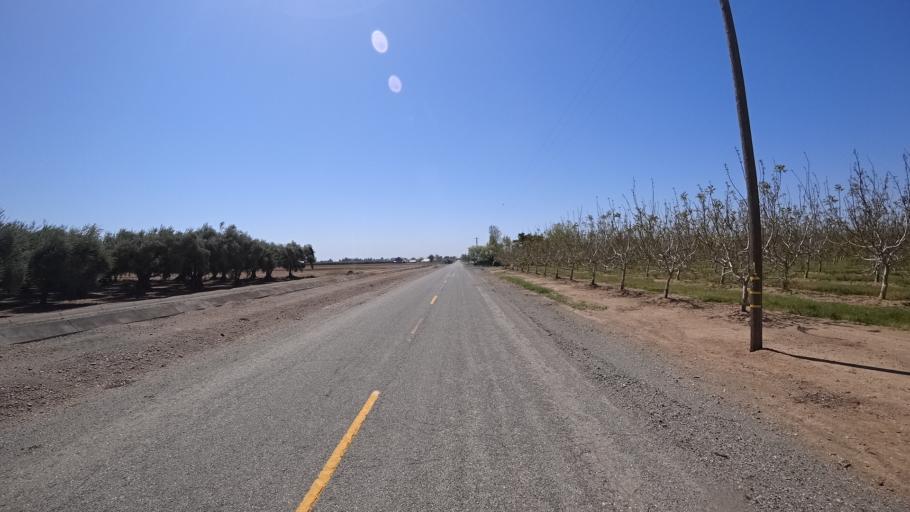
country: US
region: California
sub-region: Glenn County
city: Orland
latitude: 39.7822
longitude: -122.1690
